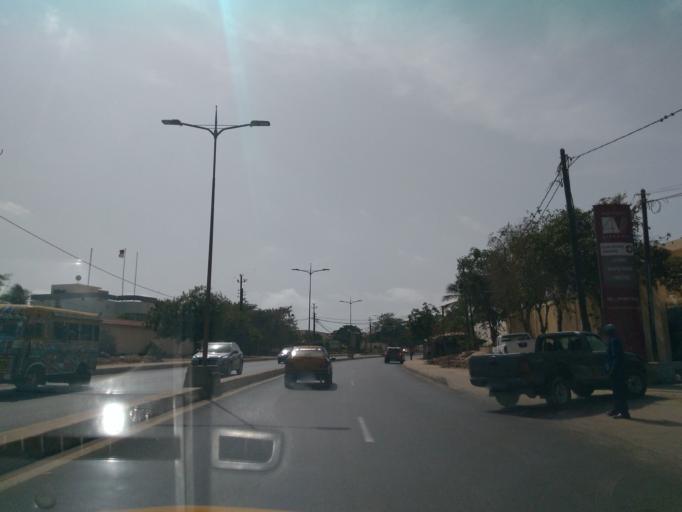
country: SN
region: Dakar
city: Mermoz Boabab
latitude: 14.7041
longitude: -17.4770
